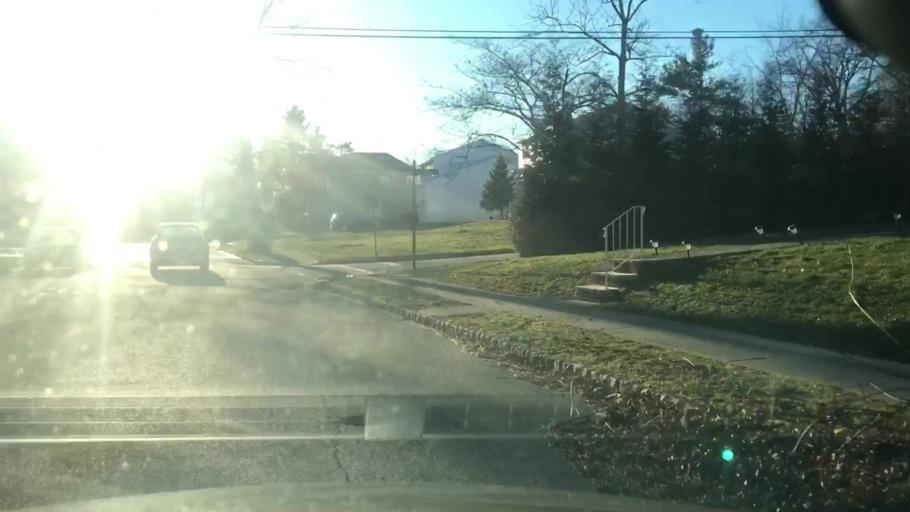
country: US
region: New Jersey
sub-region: Essex County
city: Northfield
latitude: 40.7772
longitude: -74.3052
